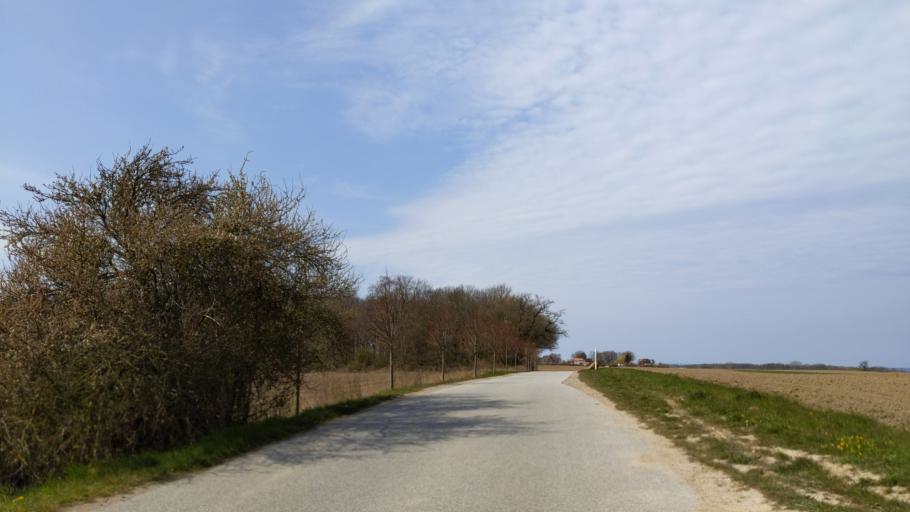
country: DE
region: Mecklenburg-Vorpommern
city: Dassow
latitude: 53.9548
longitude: 10.9492
